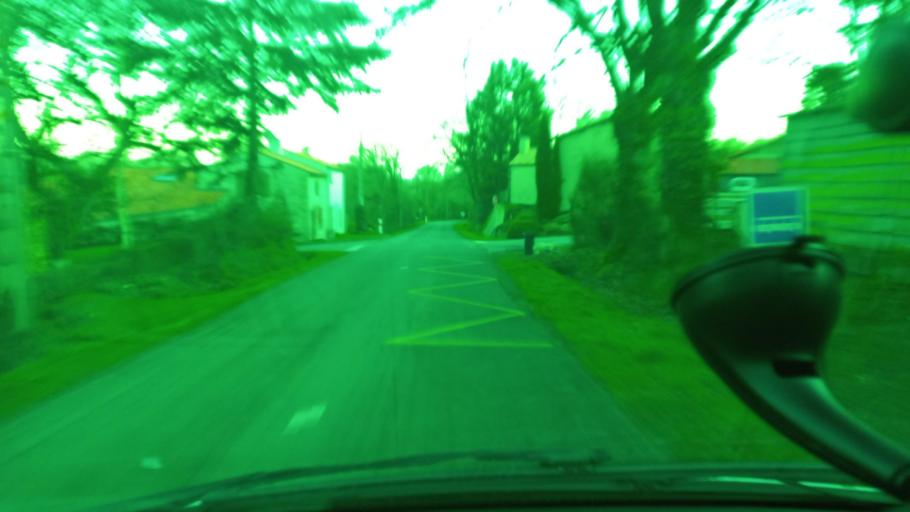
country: FR
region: Pays de la Loire
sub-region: Departement de la Vendee
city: Belleville-sur-Vie
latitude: 46.7935
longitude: -1.4102
